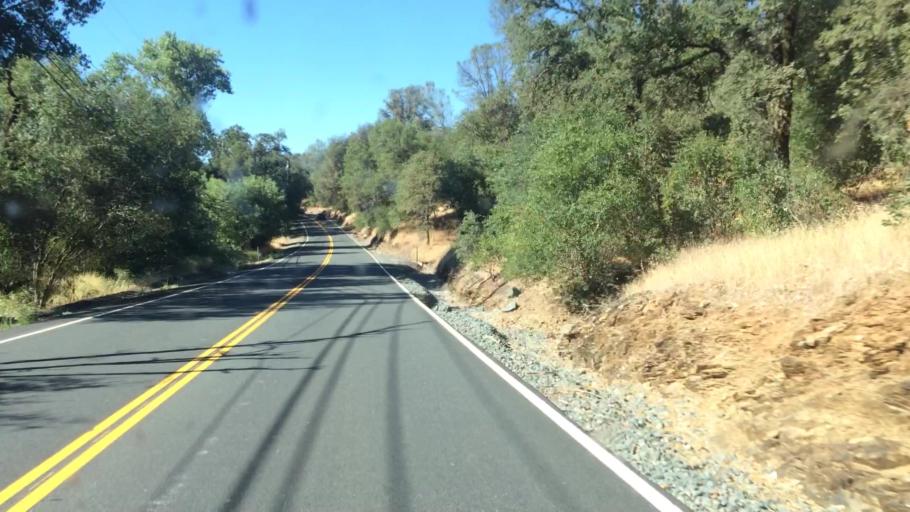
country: US
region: California
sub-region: Amador County
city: Plymouth
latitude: 38.5689
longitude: -120.8460
